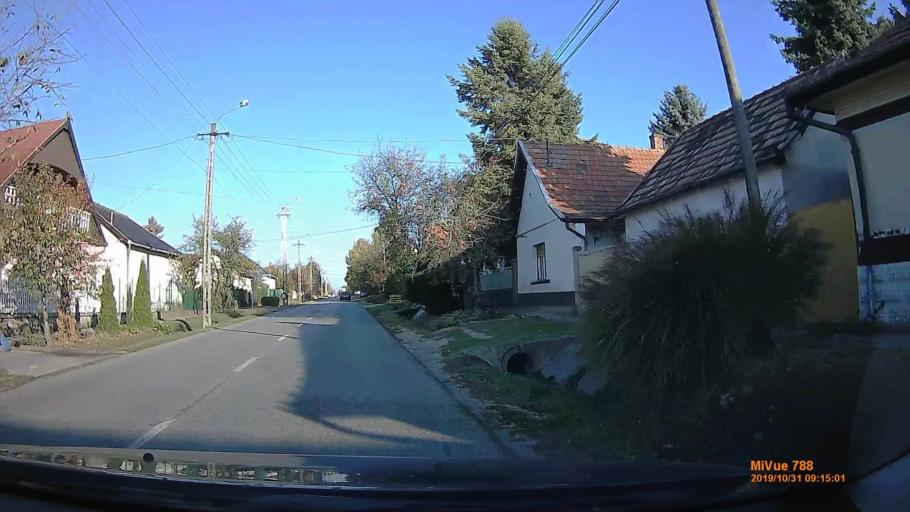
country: HU
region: Pest
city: Peteri
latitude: 47.3902
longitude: 19.4091
